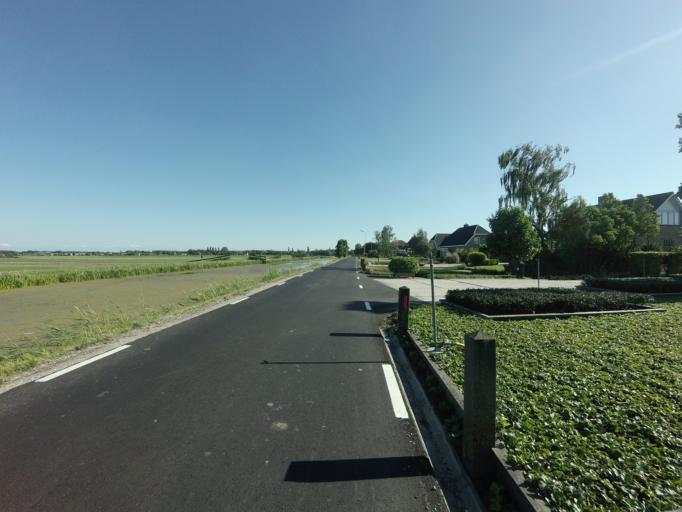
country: NL
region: South Holland
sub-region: Gemeente Waddinxveen
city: Oranjewijk
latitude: 52.0510
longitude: 4.6795
